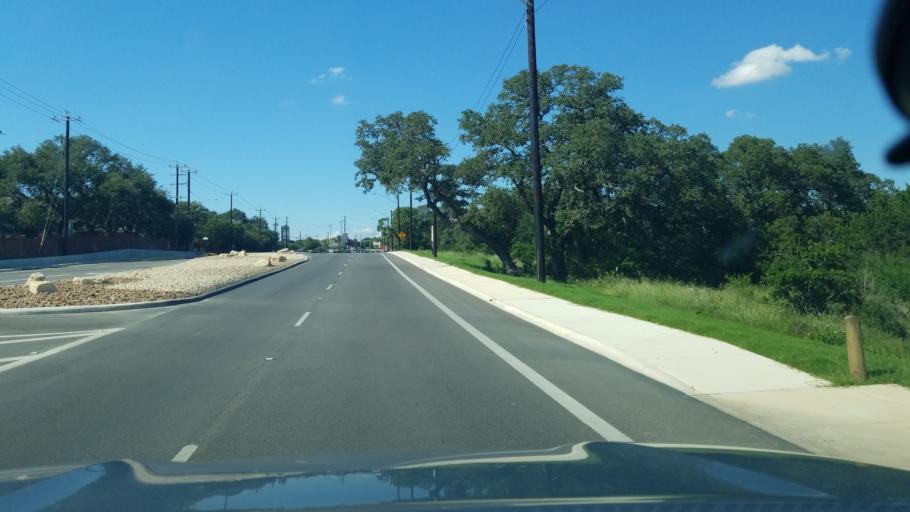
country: US
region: Texas
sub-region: Bexar County
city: Hollywood Park
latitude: 29.5993
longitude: -98.4411
